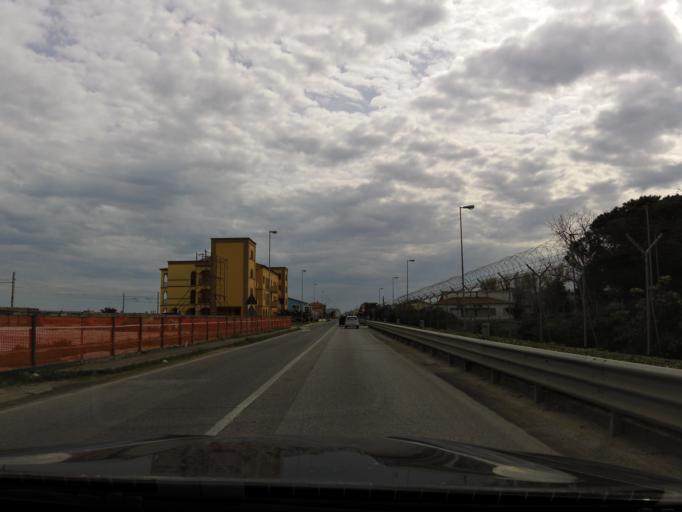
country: IT
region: The Marches
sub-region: Provincia di Macerata
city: Porto Potenza Picena
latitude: 43.3803
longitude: 13.6884
